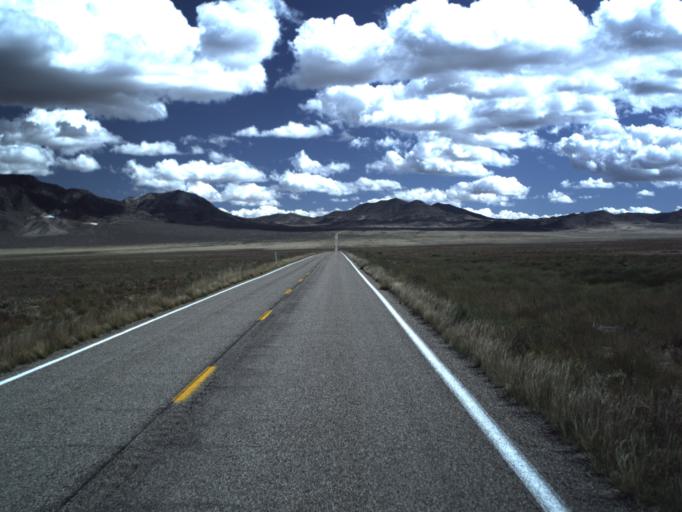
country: US
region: Utah
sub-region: Beaver County
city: Milford
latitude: 38.4671
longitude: -113.3968
